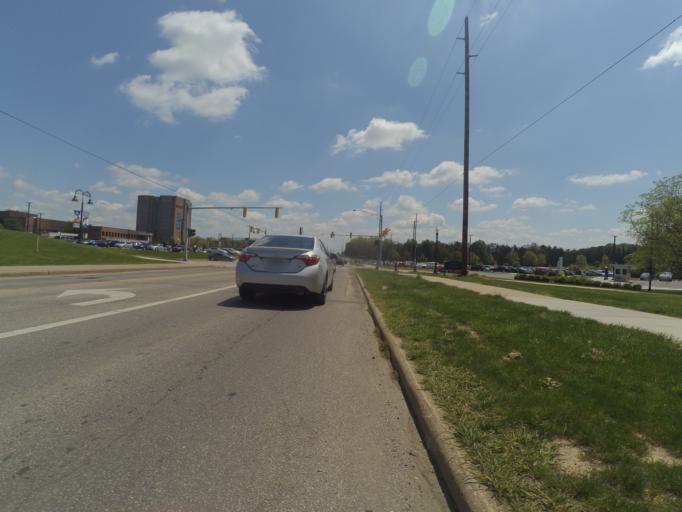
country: US
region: Ohio
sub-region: Portage County
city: Kent
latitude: 41.1472
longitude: -81.3469
